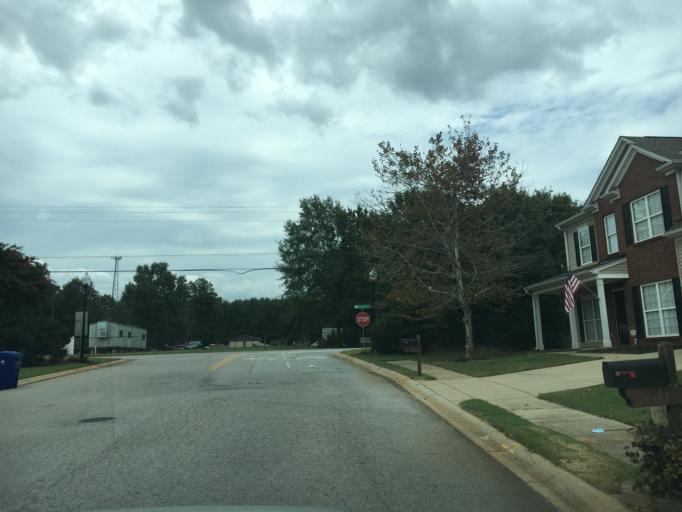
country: US
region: South Carolina
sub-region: Spartanburg County
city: Duncan
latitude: 34.8957
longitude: -82.1285
